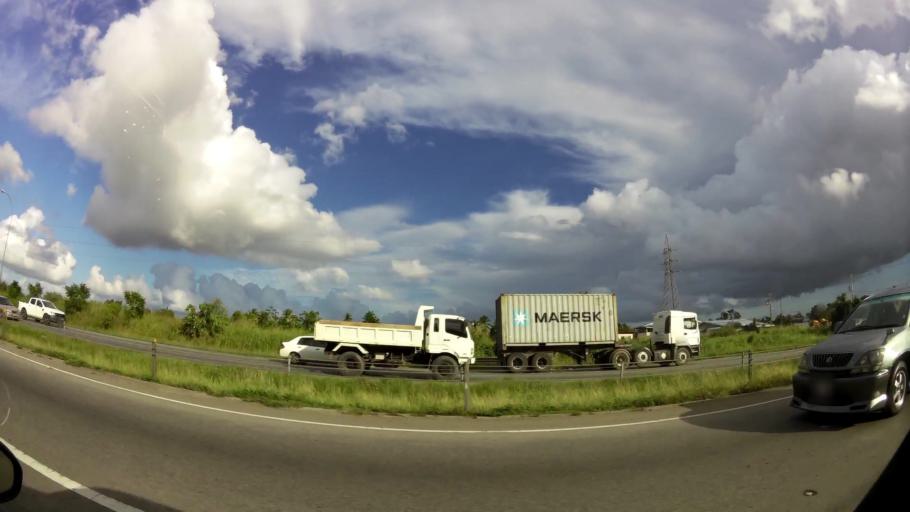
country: TT
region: Chaguanas
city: Chaguanas
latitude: 10.4735
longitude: -61.4051
